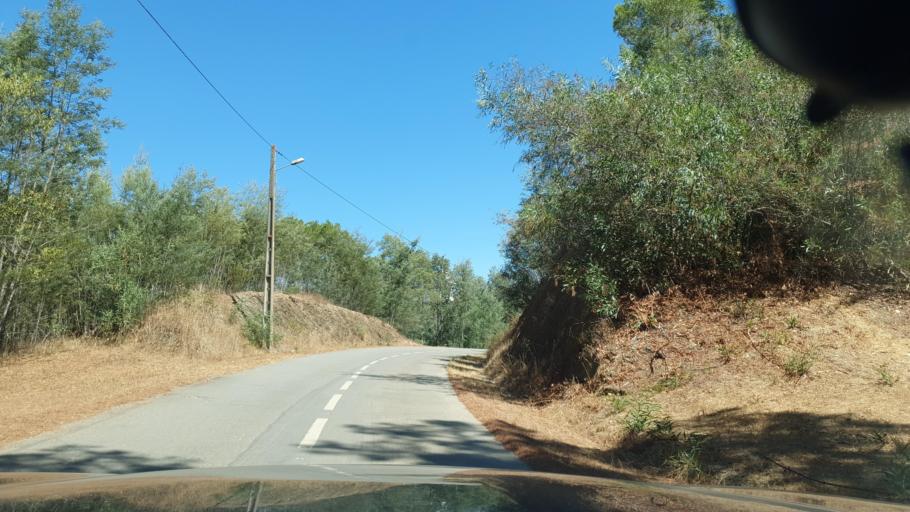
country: PT
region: Beja
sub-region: Odemira
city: Odemira
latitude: 37.5085
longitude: -8.4383
